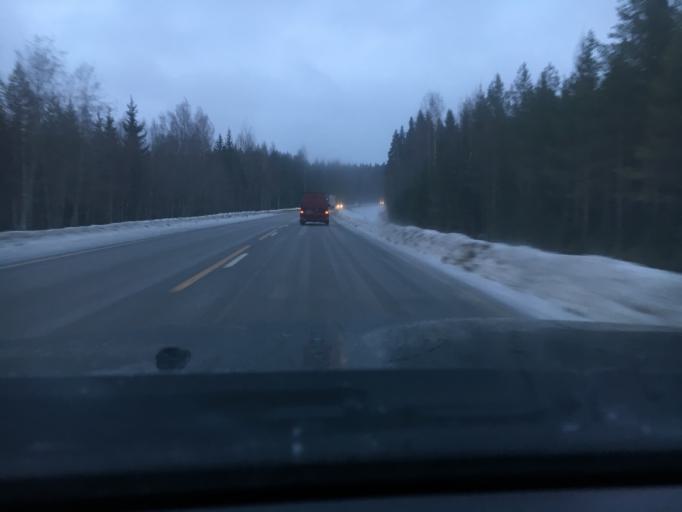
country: FI
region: Northern Savo
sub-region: Sisae-Savo
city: Rautalampi
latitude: 62.4186
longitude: 26.7137
